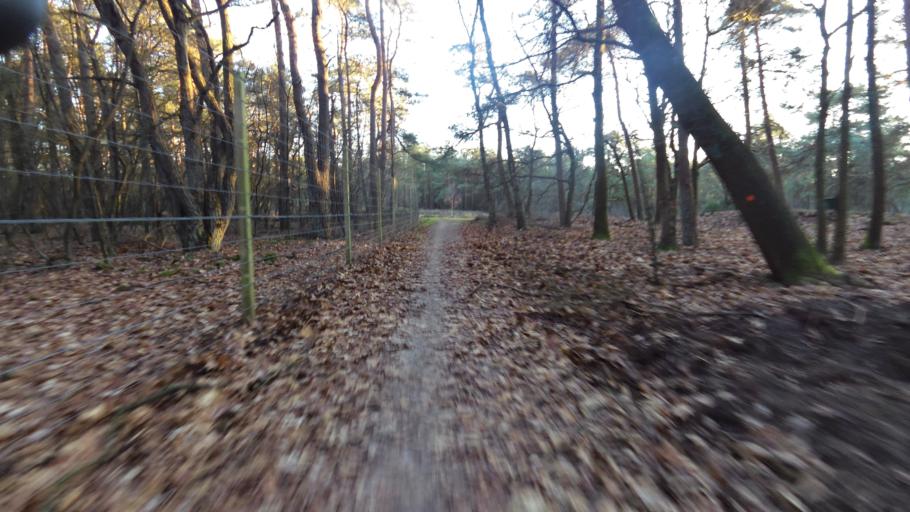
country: NL
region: Gelderland
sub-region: Gemeente Barneveld
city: Garderen
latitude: 52.2091
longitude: 5.7540
